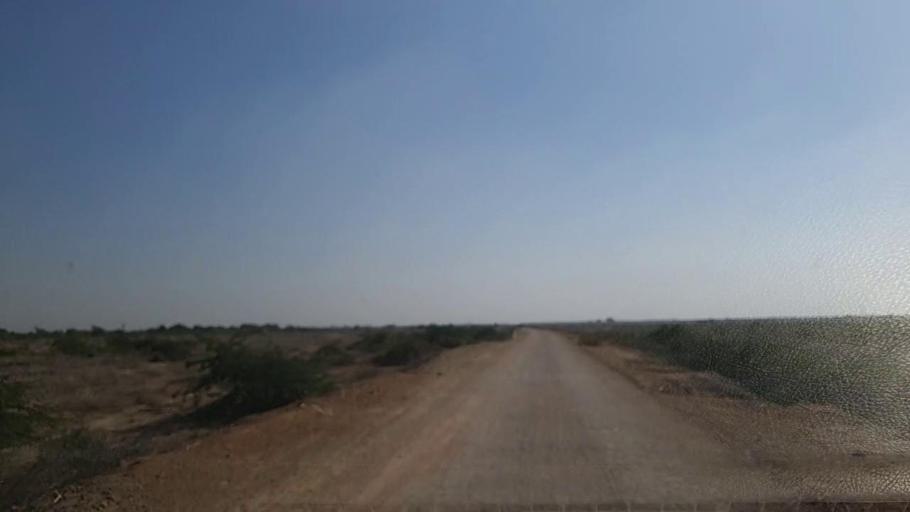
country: PK
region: Sindh
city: Daro Mehar
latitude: 24.8073
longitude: 68.0758
